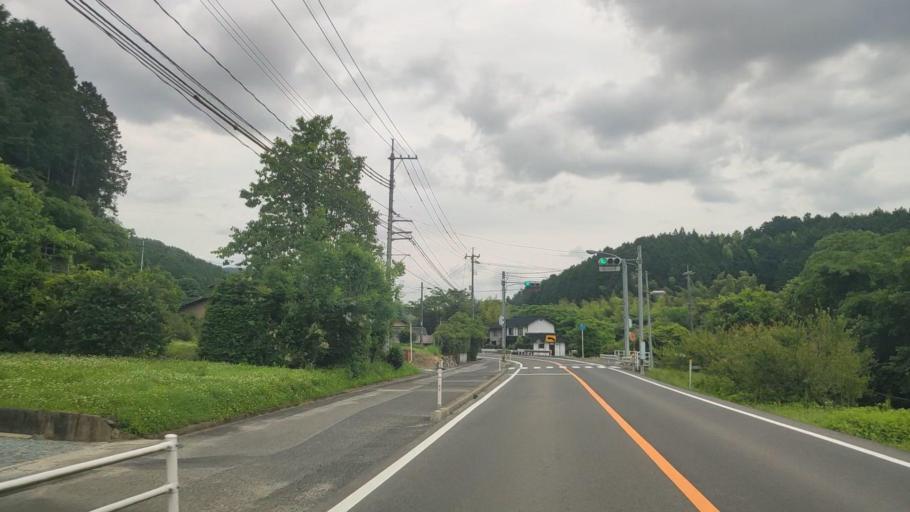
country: JP
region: Okayama
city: Tsuyama
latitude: 35.0623
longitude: 133.8365
